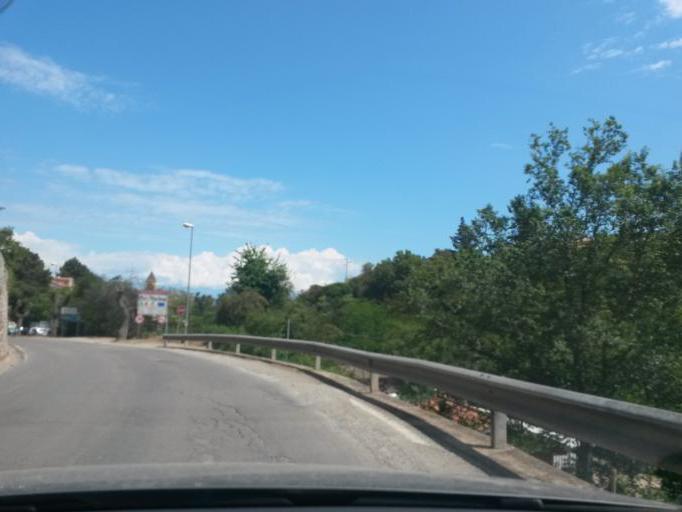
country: IT
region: Tuscany
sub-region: Provincia di Livorno
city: Rio Marina
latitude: 42.8135
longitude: 10.4198
